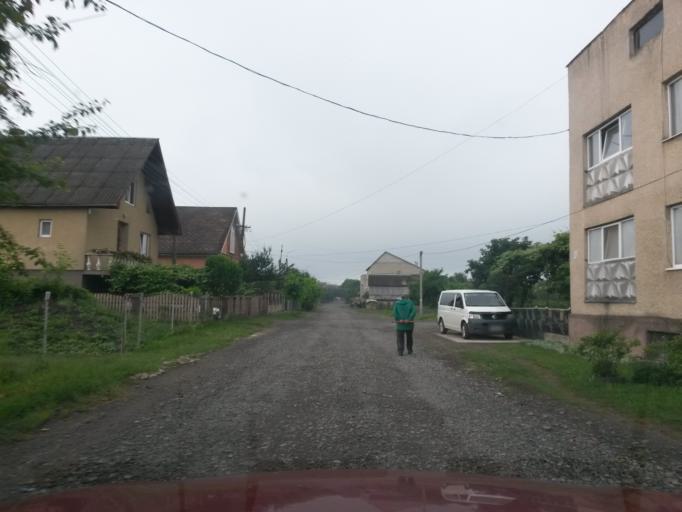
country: UA
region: Zakarpattia
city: Velykyi Bereznyi
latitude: 48.9070
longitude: 22.4637
